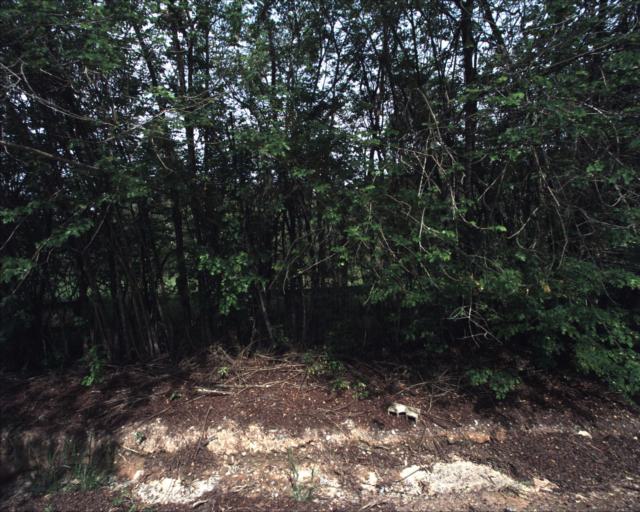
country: BR
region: Sao Paulo
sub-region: Salto De Pirapora
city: Salto de Pirapora
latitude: -23.5629
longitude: -47.5363
